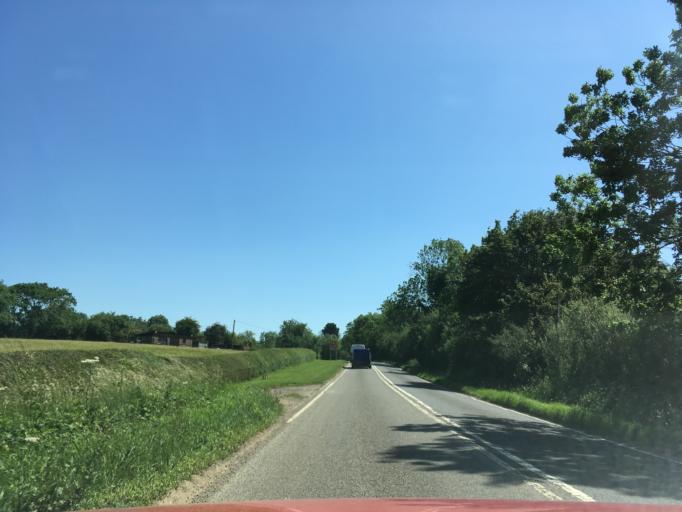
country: GB
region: England
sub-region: Northamptonshire
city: Brackley
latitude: 51.9971
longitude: -1.1840
